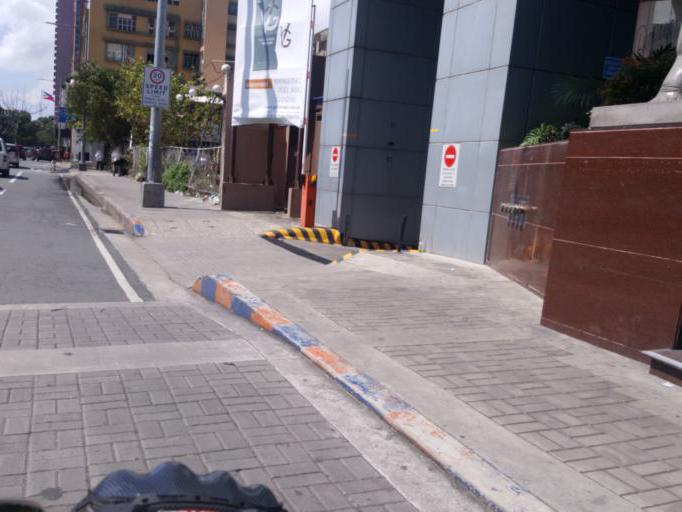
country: PH
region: Metro Manila
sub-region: City of Manila
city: Port Area
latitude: 14.5767
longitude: 120.9794
